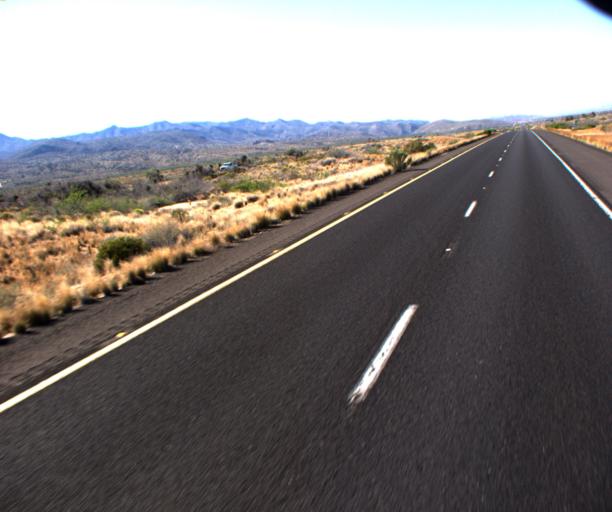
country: US
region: Arizona
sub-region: Mohave County
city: Kingman
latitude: 35.0711
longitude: -113.6659
